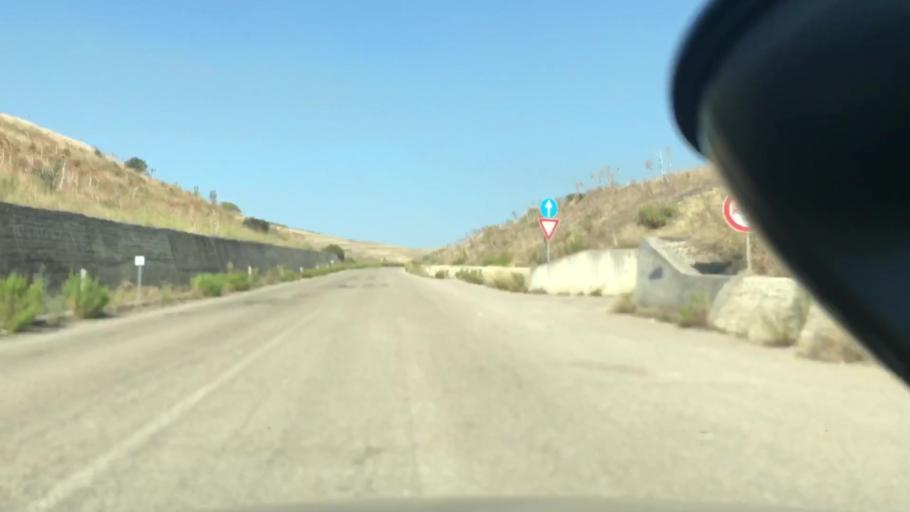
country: IT
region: Basilicate
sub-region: Provincia di Matera
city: Grottole
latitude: 40.6934
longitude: 16.4317
